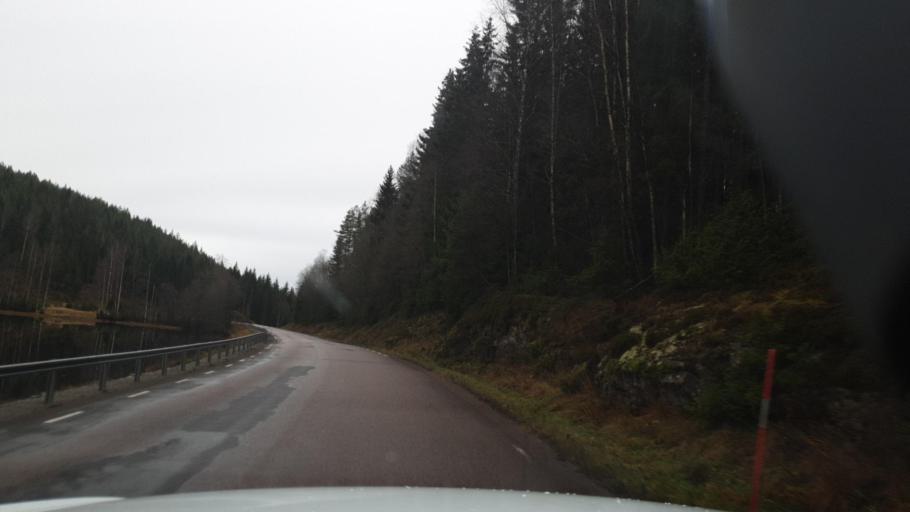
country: SE
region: Vaermland
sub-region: Arvika Kommun
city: Arvika
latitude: 59.7006
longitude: 12.7912
